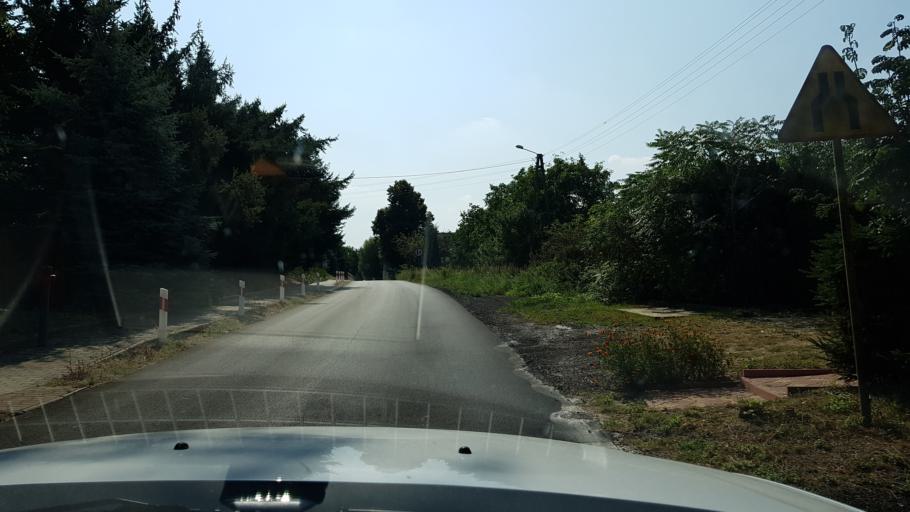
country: PL
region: West Pomeranian Voivodeship
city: Trzcinsko Zdroj
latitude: 52.9231
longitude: 14.5330
